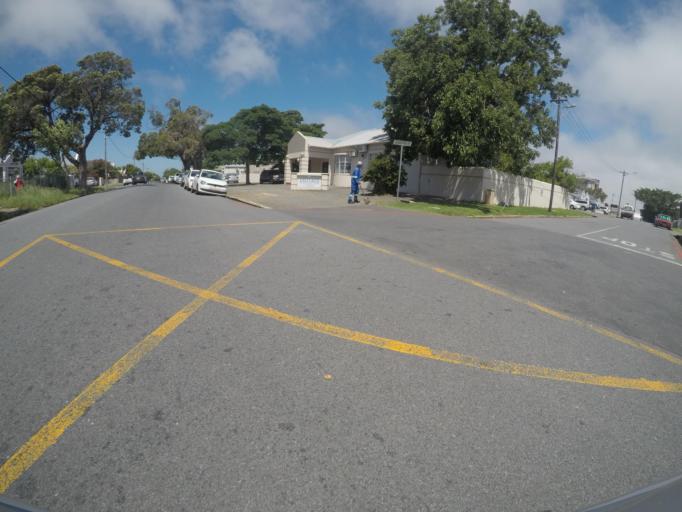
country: ZA
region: Eastern Cape
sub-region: Buffalo City Metropolitan Municipality
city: East London
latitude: -32.9788
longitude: 27.9003
